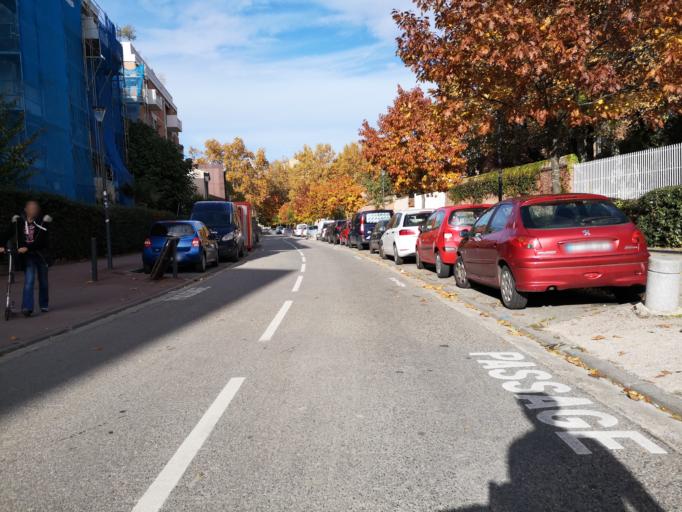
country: FR
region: Midi-Pyrenees
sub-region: Departement de la Haute-Garonne
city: Toulouse
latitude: 43.5956
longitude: 1.4414
